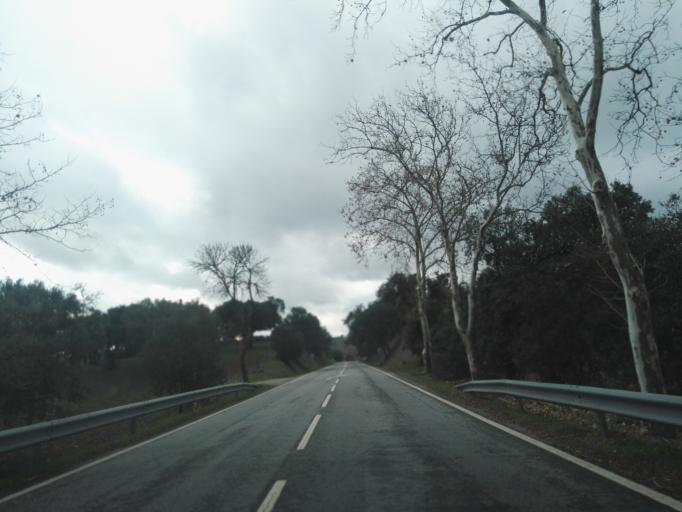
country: PT
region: Portalegre
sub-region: Arronches
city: Arronches
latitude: 39.0960
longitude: -7.2813
